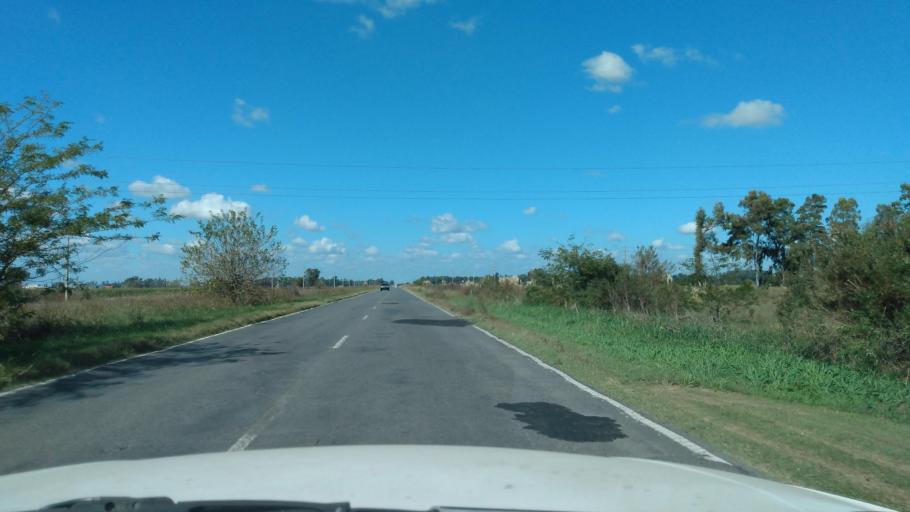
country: AR
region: Buenos Aires
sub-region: Partido de Mercedes
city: Mercedes
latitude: -34.7208
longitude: -59.3945
